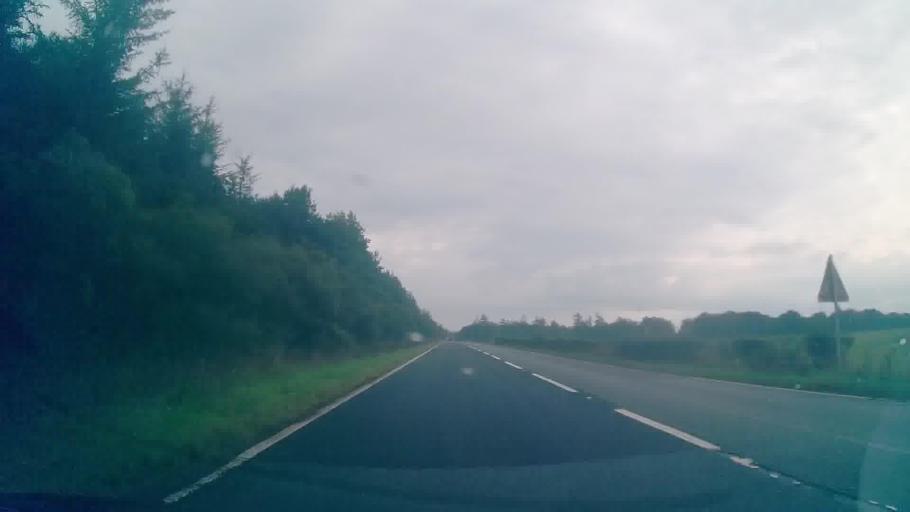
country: GB
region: Scotland
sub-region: Dumfries and Galloway
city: Annan
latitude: 55.0158
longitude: -3.3573
